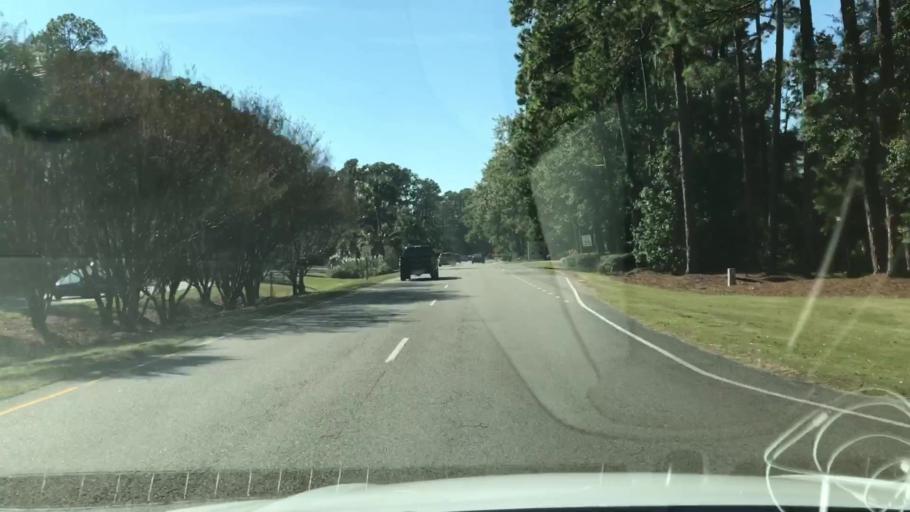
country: US
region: South Carolina
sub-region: Beaufort County
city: Hilton Head Island
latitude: 32.1586
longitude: -80.7549
